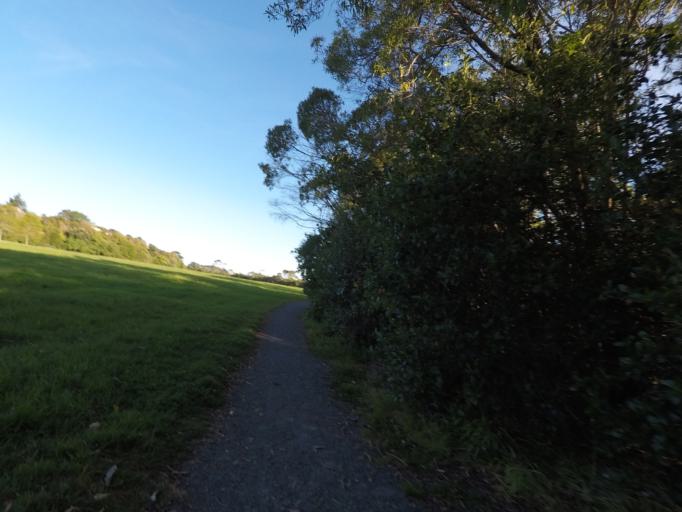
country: NZ
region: Auckland
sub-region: Auckland
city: Rosebank
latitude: -36.8413
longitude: 174.6329
